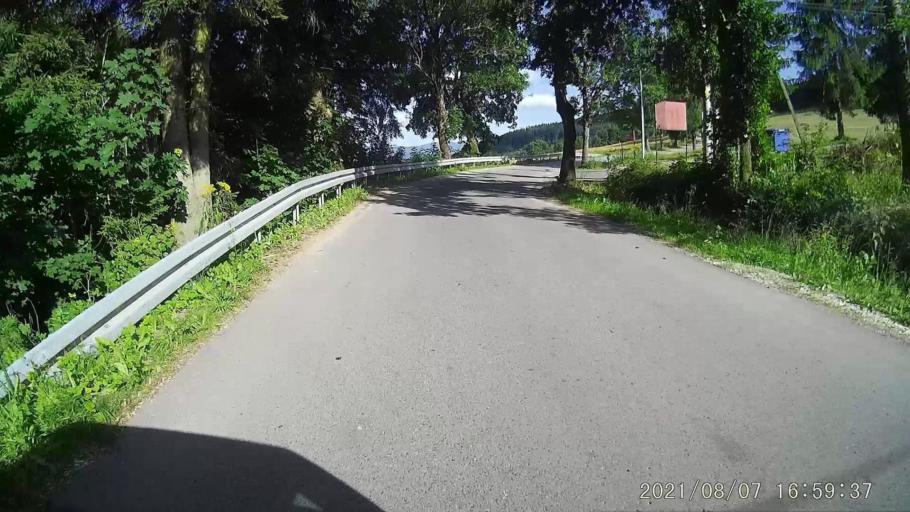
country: PL
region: Lower Silesian Voivodeship
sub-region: Powiat klodzki
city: Bystrzyca Klodzka
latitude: 50.2874
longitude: 16.5457
